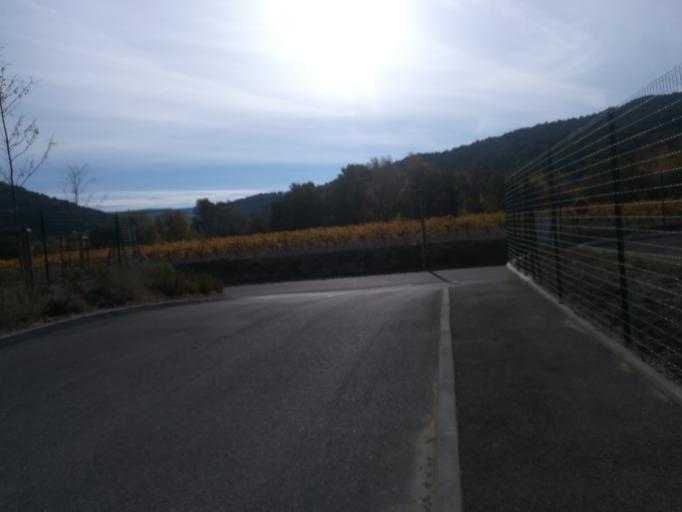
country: FR
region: Provence-Alpes-Cote d'Azur
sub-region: Departement du Vaucluse
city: Vaison-la-Romaine
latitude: 44.2445
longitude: 5.0435
